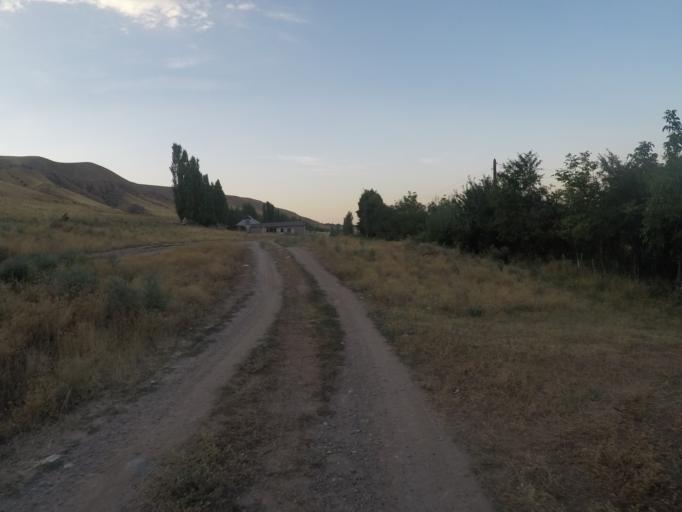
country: KG
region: Chuy
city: Bishkek
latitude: 42.7713
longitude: 74.6396
